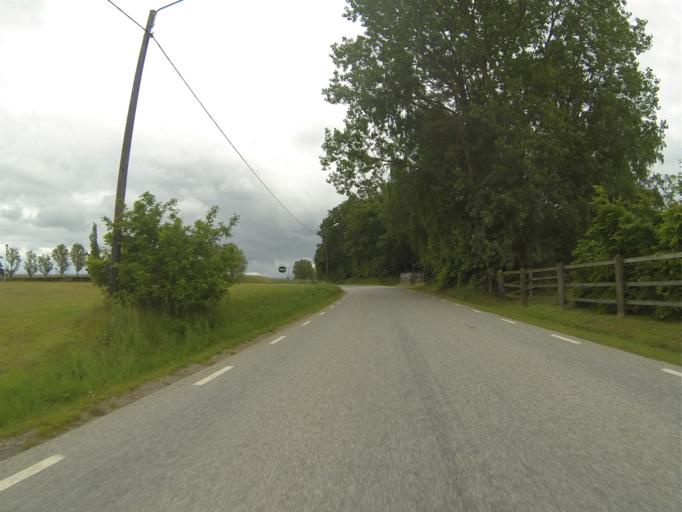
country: SE
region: Skane
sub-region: Lunds Kommun
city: Genarp
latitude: 55.7108
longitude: 13.3664
